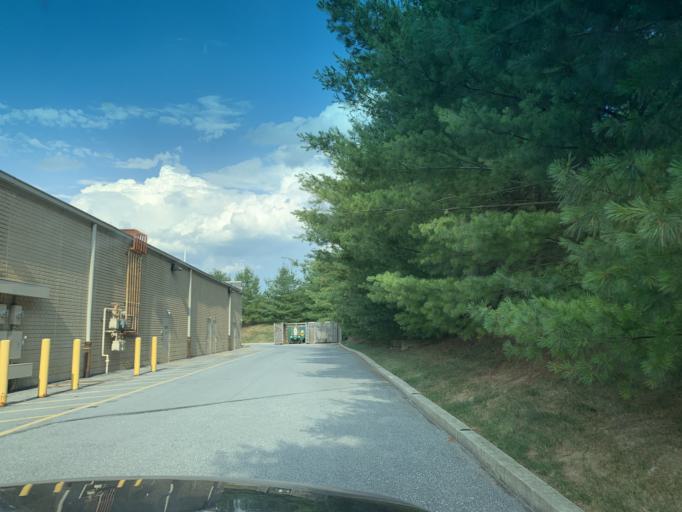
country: US
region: Pennsylvania
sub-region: Dauphin County
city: Progress
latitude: 40.3024
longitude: -76.8436
